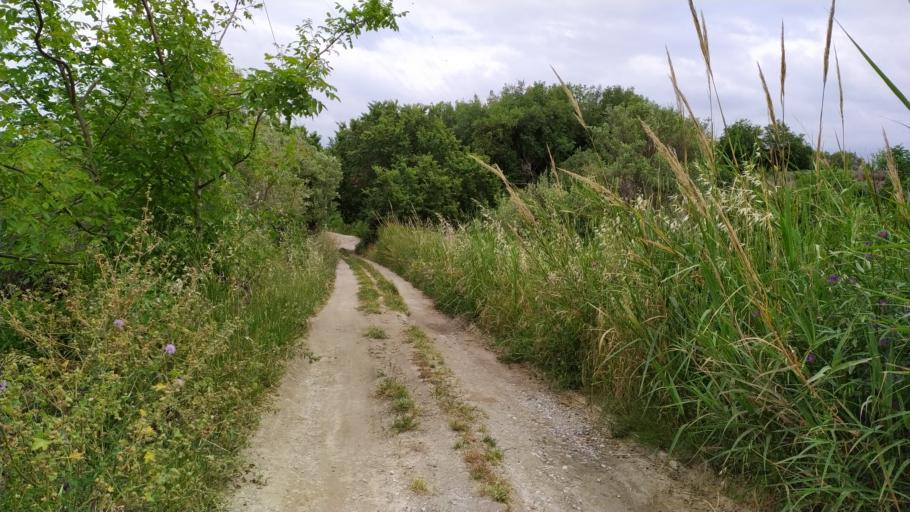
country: IT
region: Sicily
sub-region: Messina
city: Gualtieri Sicamino
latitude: 38.1575
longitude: 15.2978
